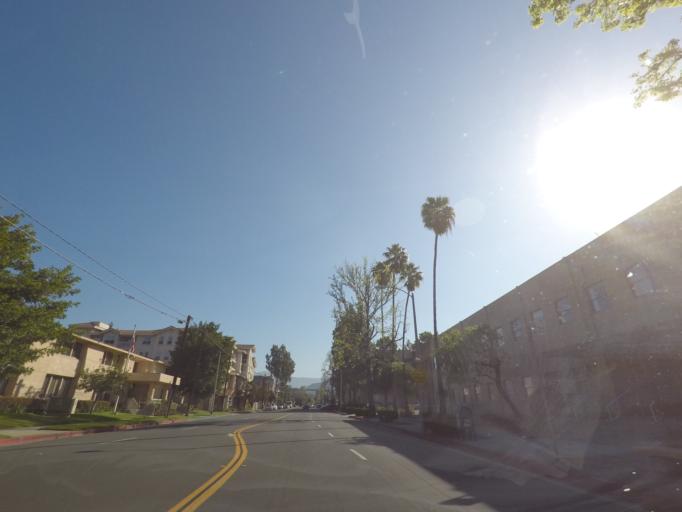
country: US
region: California
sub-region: Los Angeles County
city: Glendale
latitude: 34.1523
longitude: -118.2315
